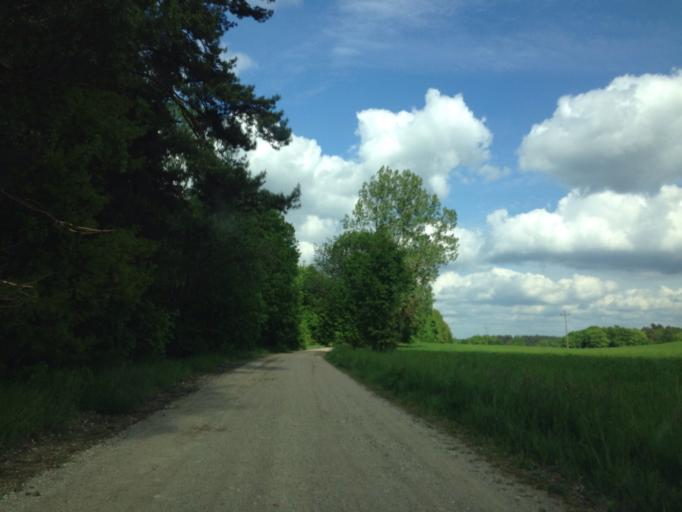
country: PL
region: Warmian-Masurian Voivodeship
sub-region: Powiat nidzicki
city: Nidzica
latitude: 53.4728
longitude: 20.3836
